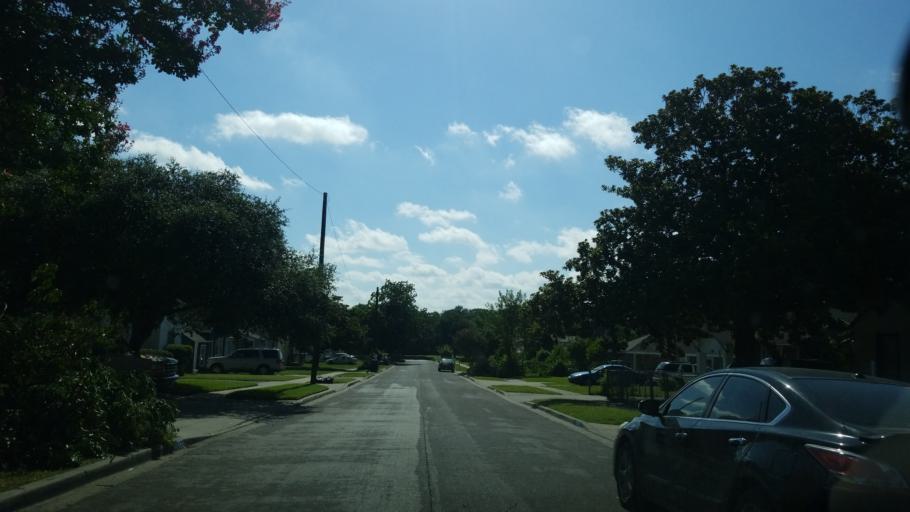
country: US
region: Texas
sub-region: Dallas County
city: Dallas
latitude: 32.7180
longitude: -96.8024
